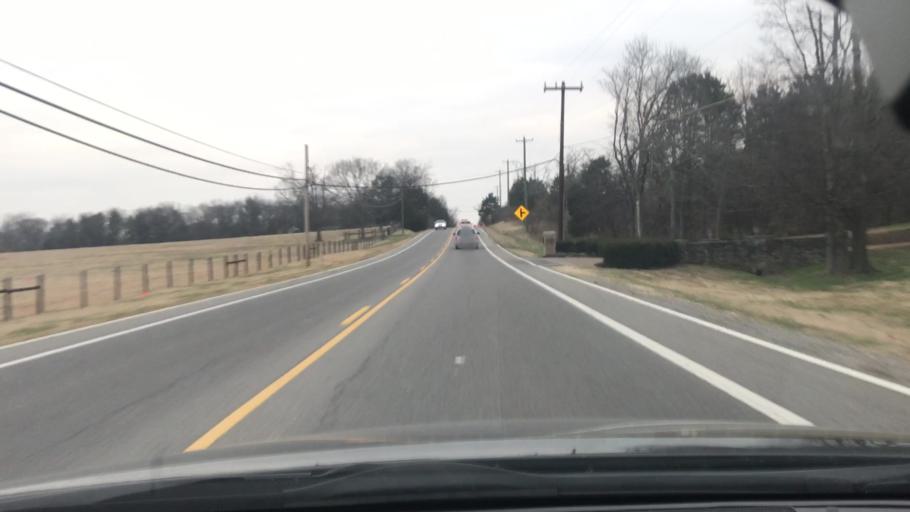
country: US
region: Tennessee
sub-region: Davidson County
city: Forest Hills
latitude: 36.0379
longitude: -86.8708
